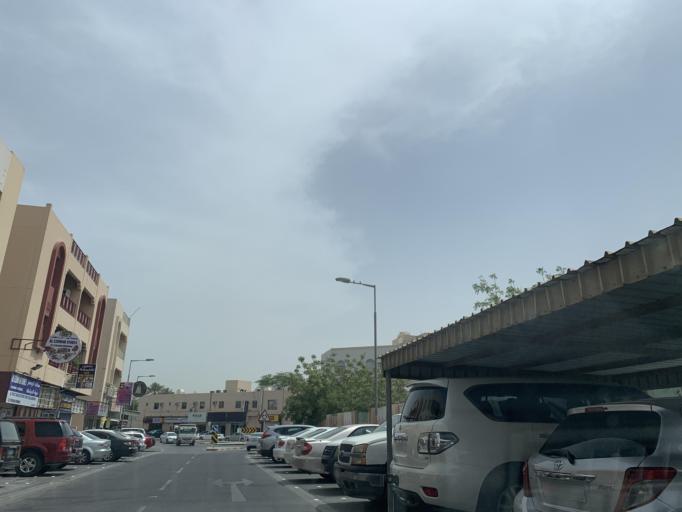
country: BH
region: Northern
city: Ar Rifa'
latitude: 26.1334
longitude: 50.5648
